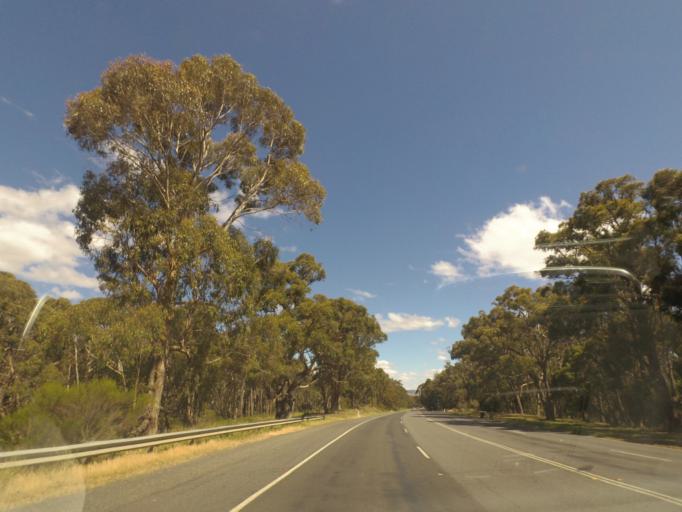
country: AU
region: Victoria
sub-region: Hume
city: Sunbury
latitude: -37.4197
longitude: 144.5527
